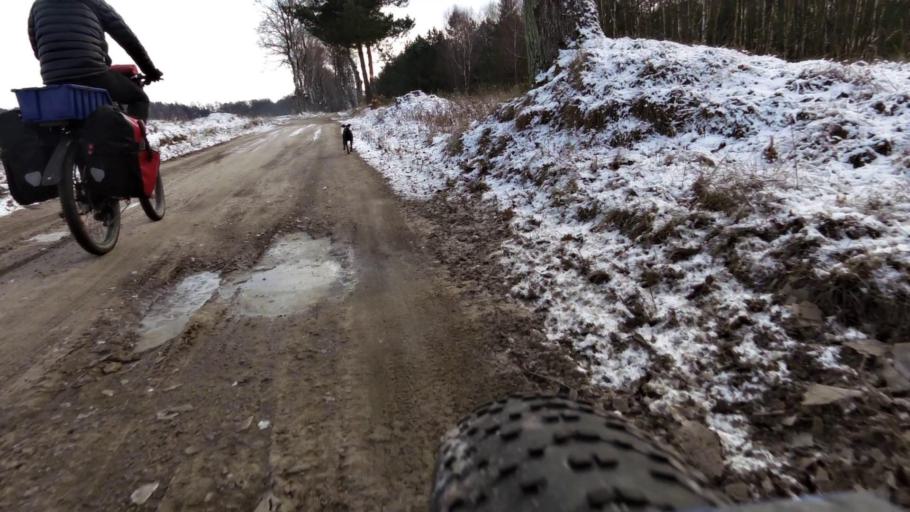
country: PL
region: West Pomeranian Voivodeship
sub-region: Powiat walecki
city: Walcz
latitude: 53.2683
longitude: 16.3105
